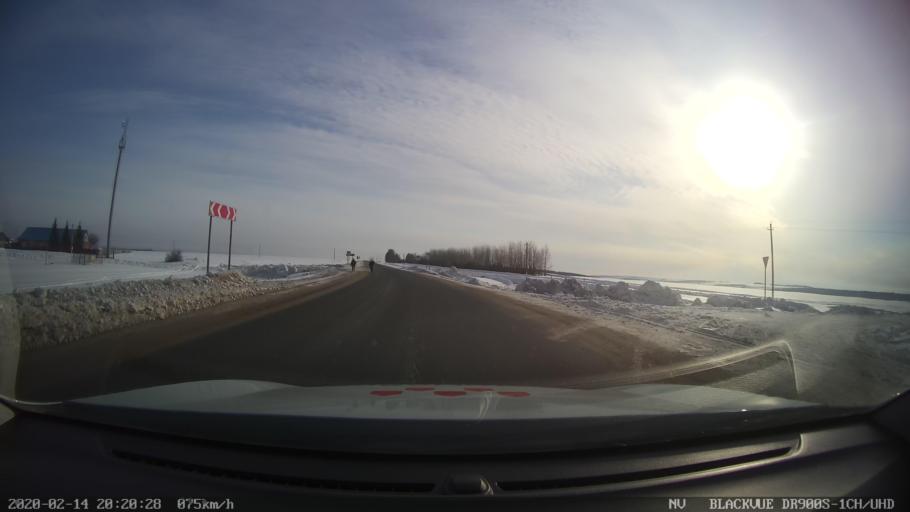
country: RU
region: Tatarstan
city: Verkhniy Uslon
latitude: 55.5571
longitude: 48.9066
